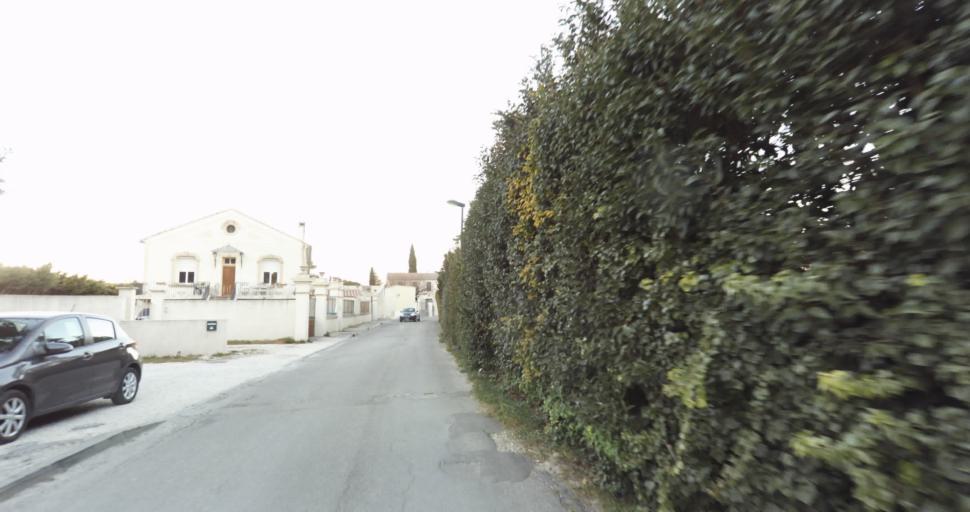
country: FR
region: Provence-Alpes-Cote d'Azur
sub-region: Departement des Bouches-du-Rhone
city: Barbentane
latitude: 43.8980
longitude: 4.7641
